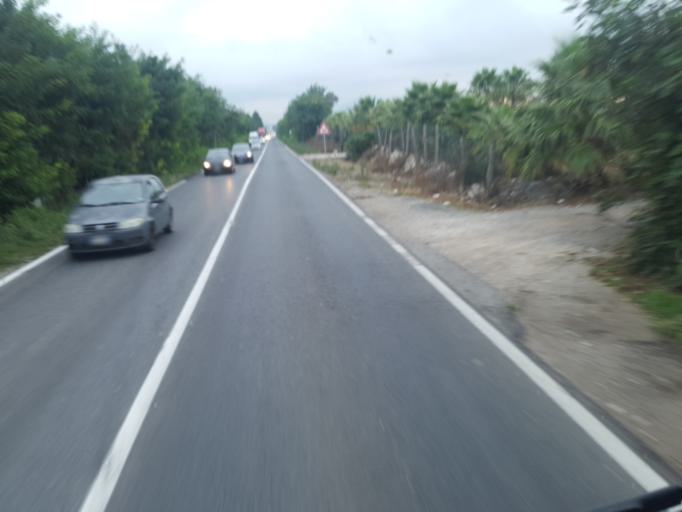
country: IT
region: Campania
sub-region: Provincia di Caserta
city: Pignataro Maggiore
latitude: 41.1695
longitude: 14.1464
